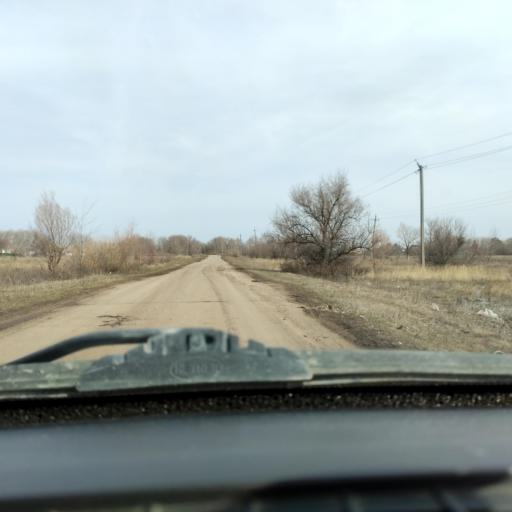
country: RU
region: Samara
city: Smyshlyayevka
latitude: 53.1758
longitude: 50.4336
